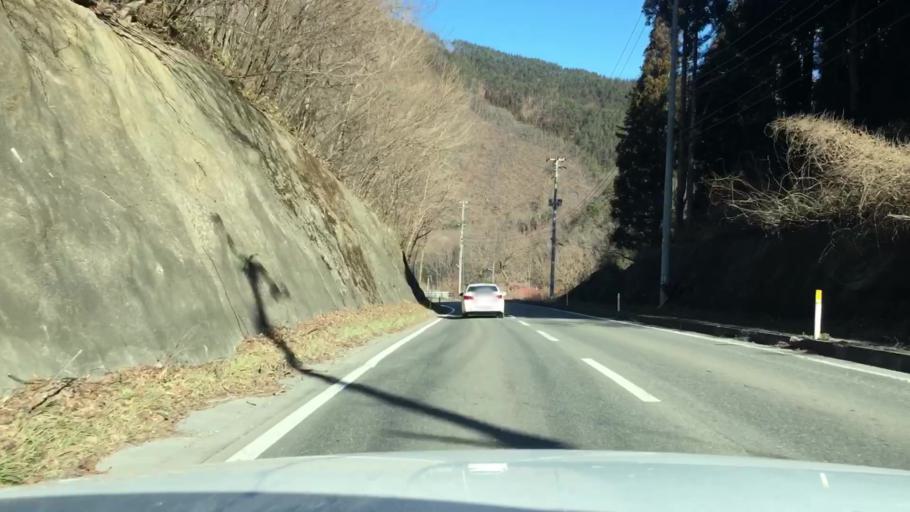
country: JP
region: Iwate
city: Miyako
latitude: 39.6215
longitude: 141.8109
